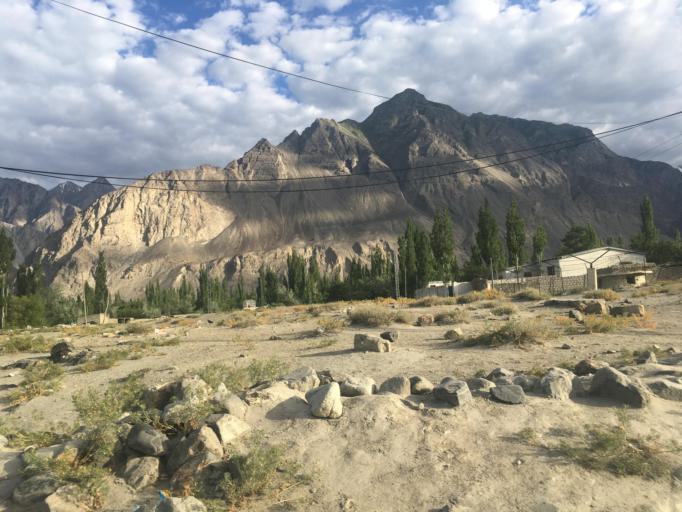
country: PK
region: Gilgit-Baltistan
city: Skardu
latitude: 35.2953
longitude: 75.6148
